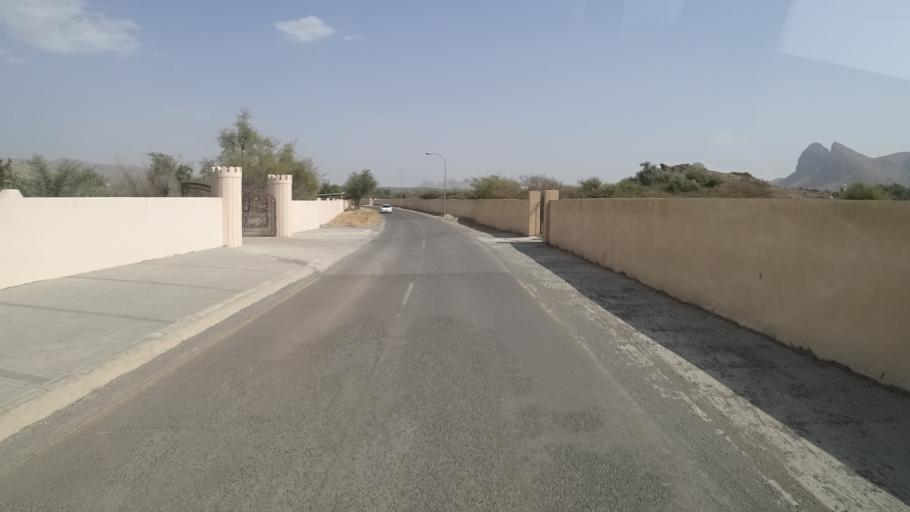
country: OM
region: Muhafazat ad Dakhiliyah
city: Bahla'
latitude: 23.1076
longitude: 57.2959
